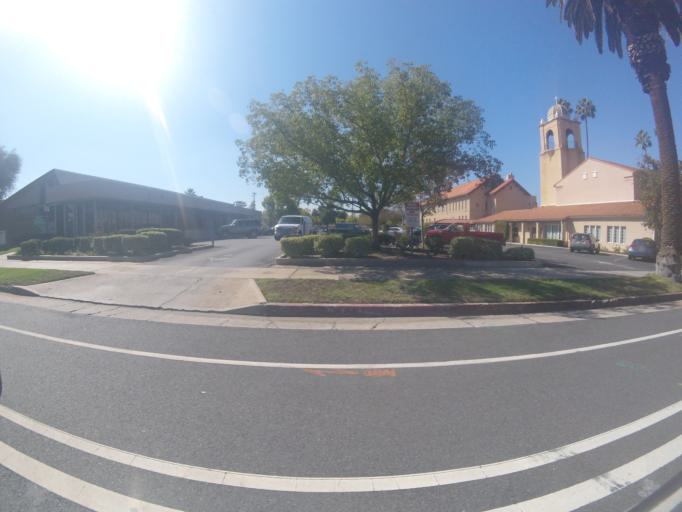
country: US
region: California
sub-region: San Bernardino County
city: Redlands
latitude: 34.0526
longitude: -117.1807
